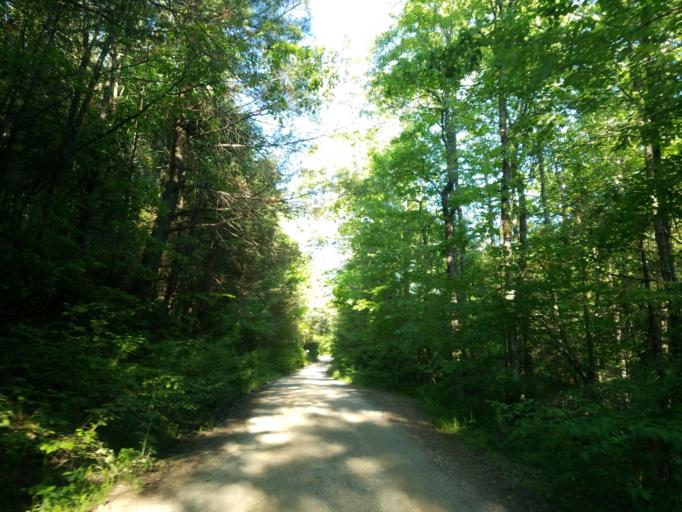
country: US
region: Georgia
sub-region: Lumpkin County
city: Dahlonega
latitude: 34.6806
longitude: -84.1374
